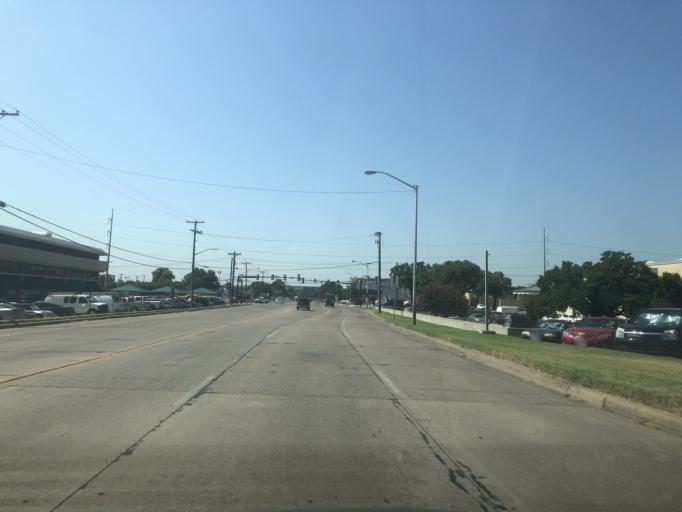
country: US
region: Texas
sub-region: Tarrant County
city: River Oaks
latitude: 32.7607
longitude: -97.3612
